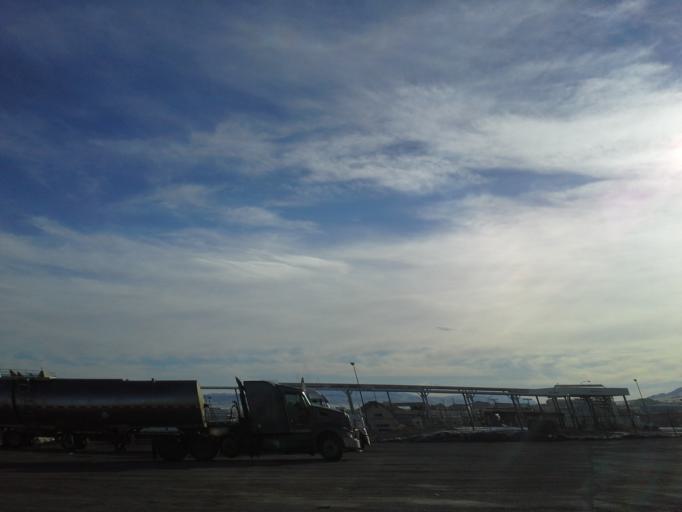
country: US
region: Montana
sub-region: Lewis and Clark County
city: Helena
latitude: 46.5923
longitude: -111.9842
